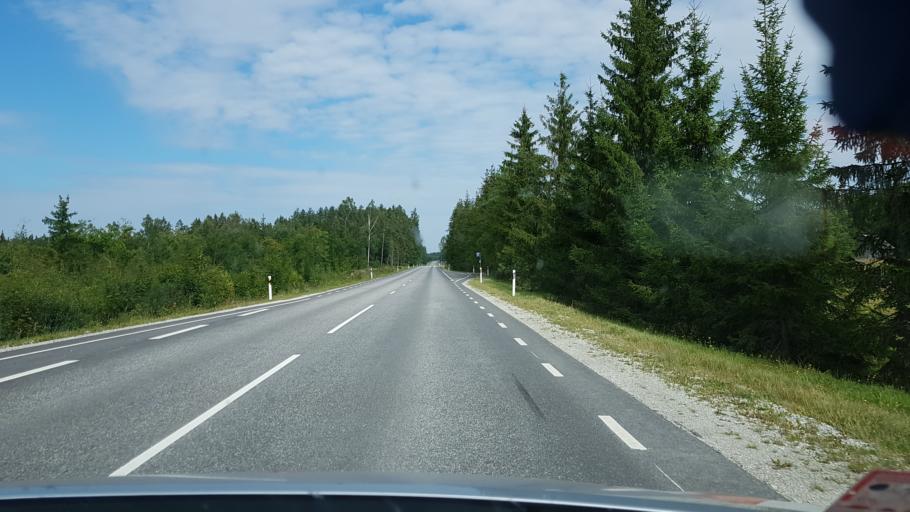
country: EE
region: Raplamaa
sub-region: Jaervakandi vald
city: Jarvakandi
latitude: 58.7200
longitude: 24.8000
